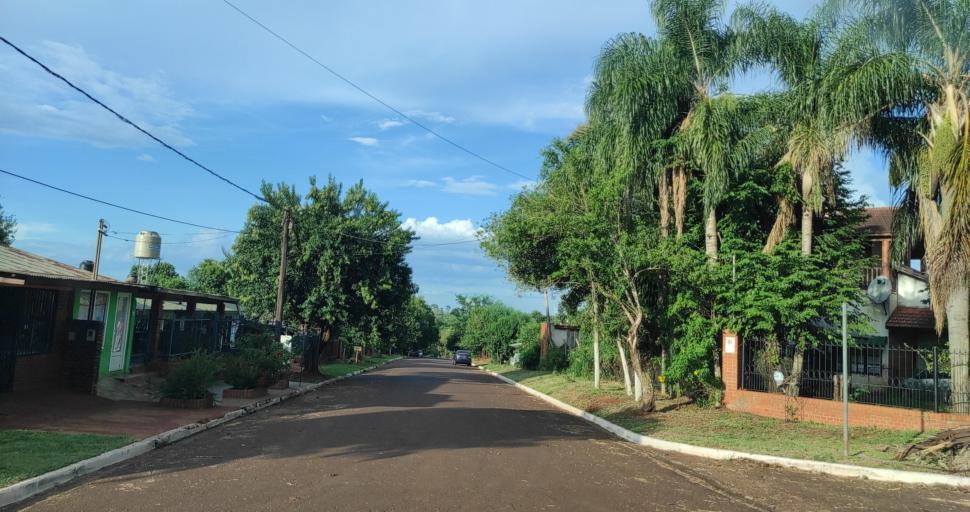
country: AR
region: Misiones
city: Santo Pipo
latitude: -27.1407
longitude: -55.4126
